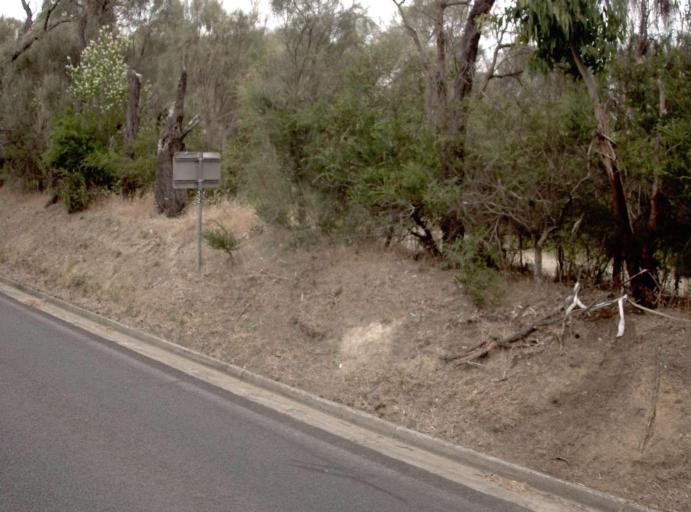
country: AU
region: Victoria
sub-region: Mornington Peninsula
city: Mount Martha
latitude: -38.2671
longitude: 145.0365
